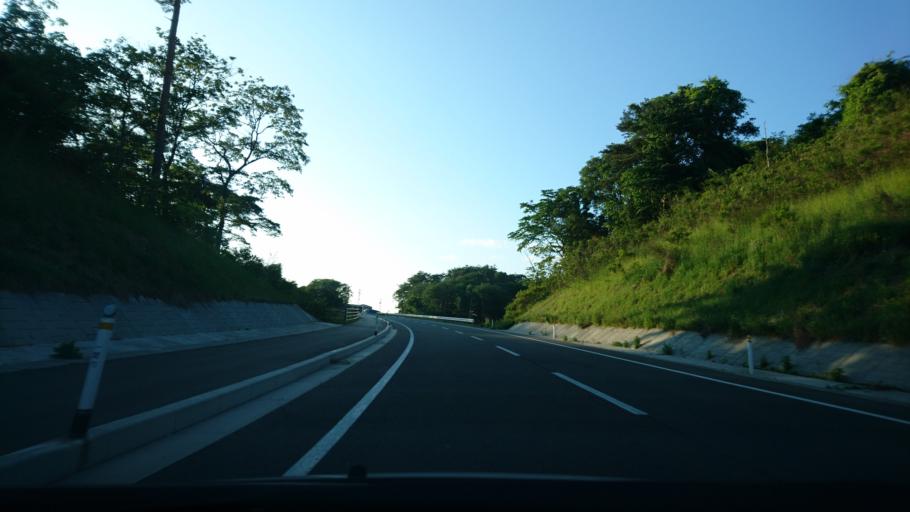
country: JP
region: Iwate
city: Ichinoseki
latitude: 38.8769
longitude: 141.1606
